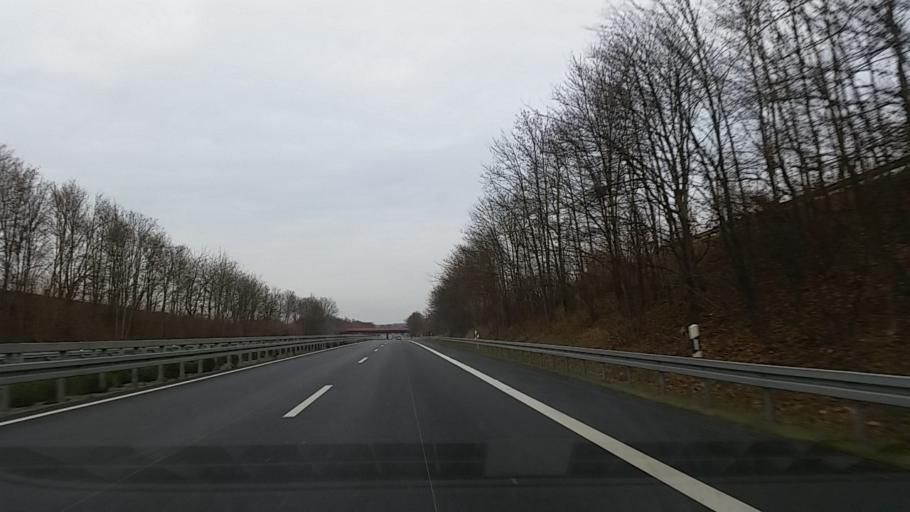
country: DE
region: Lower Saxony
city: Leiferde
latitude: 52.1964
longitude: 10.5245
